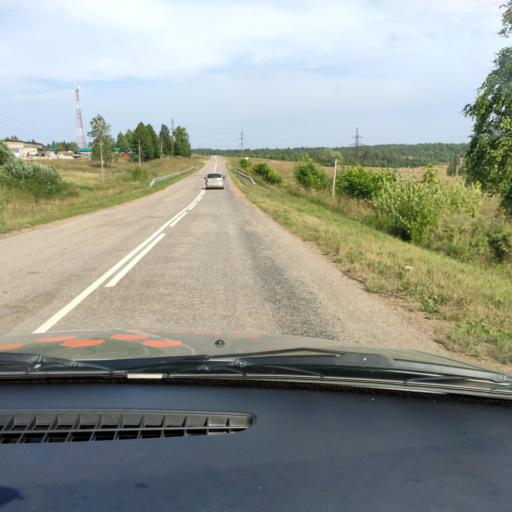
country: RU
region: Bashkortostan
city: Pavlovka
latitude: 55.3958
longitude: 56.5513
